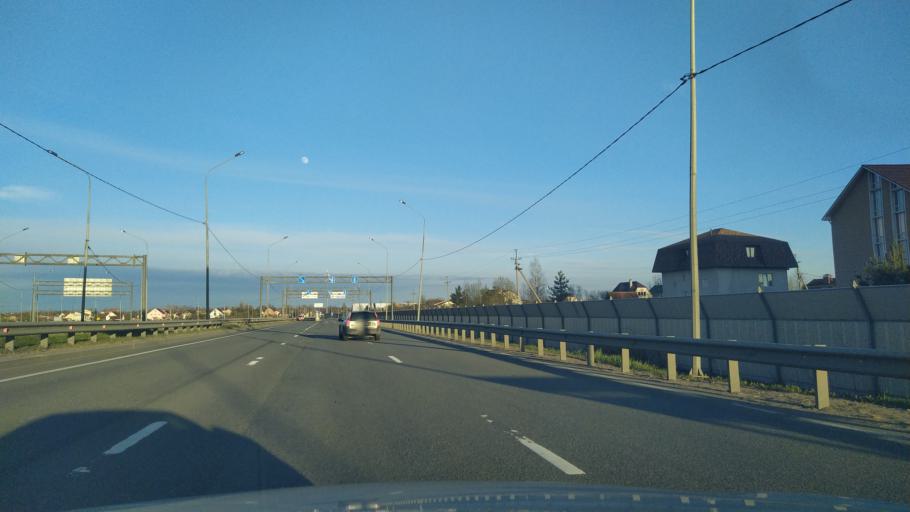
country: RU
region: St.-Petersburg
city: Aleksandrovskaya
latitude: 59.7417
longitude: 30.3176
